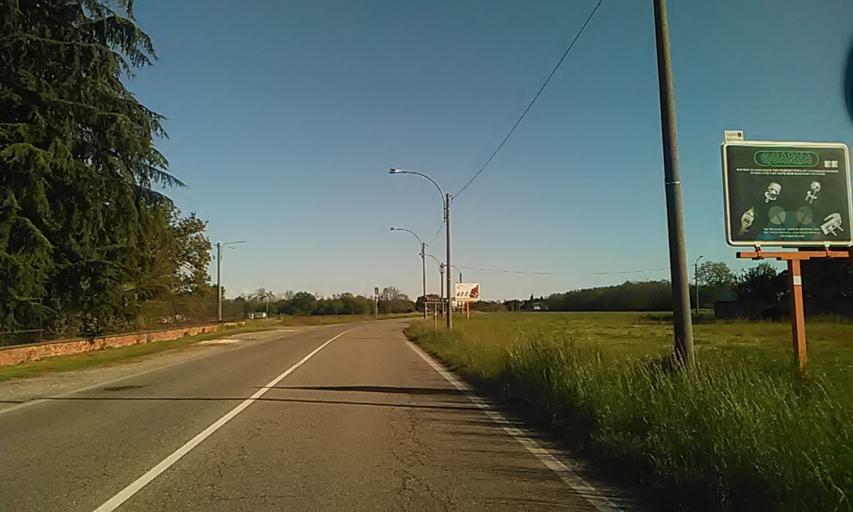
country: IT
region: Piedmont
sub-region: Provincia di Novara
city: Cavaglietto
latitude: 45.6143
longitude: 8.5192
